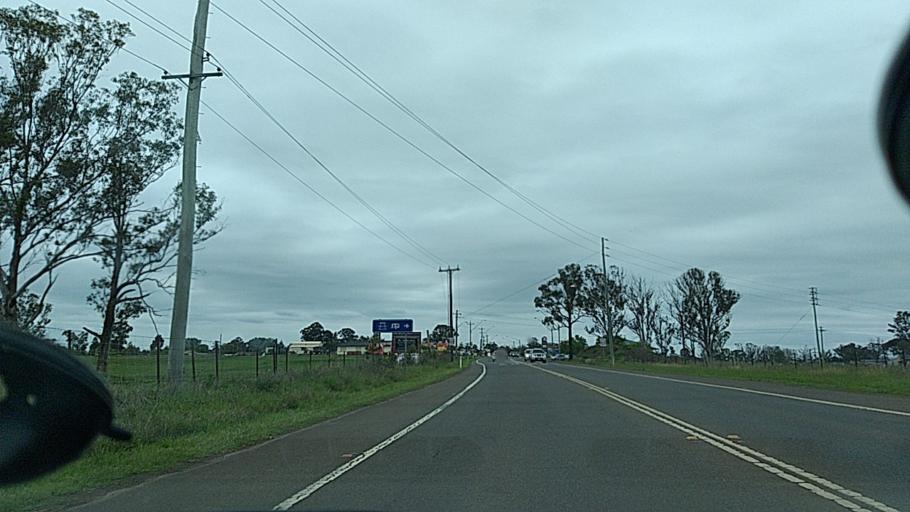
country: AU
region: New South Wales
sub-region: Liverpool
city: Luddenham
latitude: -33.8725
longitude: 150.6906
